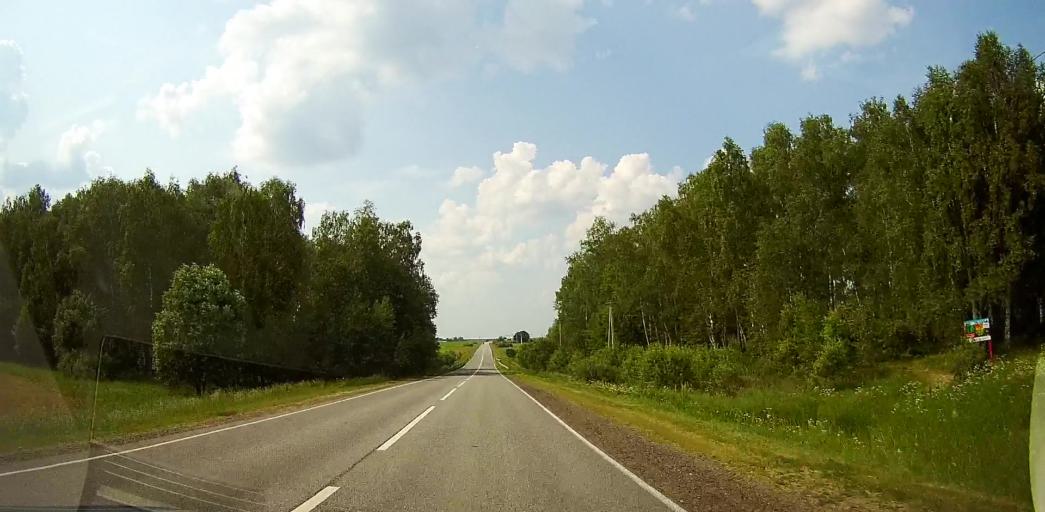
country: RU
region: Moskovskaya
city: Malino
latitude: 55.0279
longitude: 38.1695
